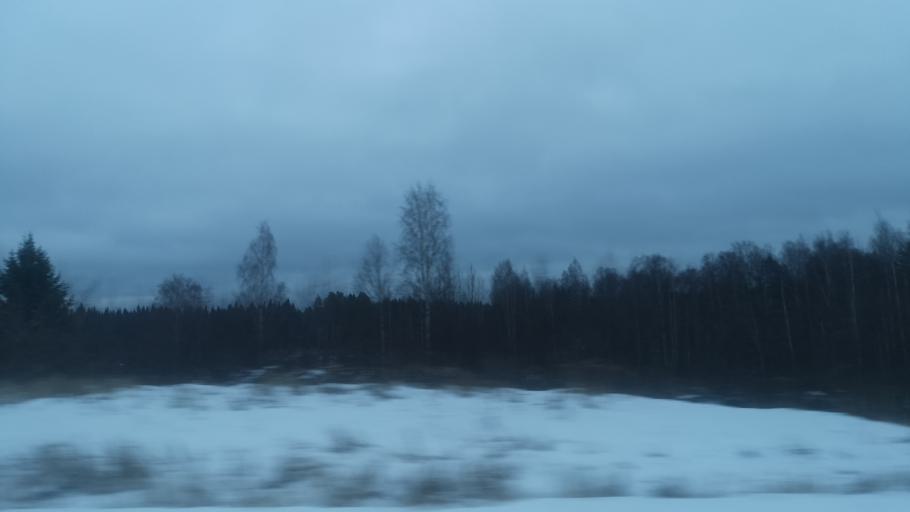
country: FI
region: Southern Savonia
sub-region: Savonlinna
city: Enonkoski
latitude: 62.1037
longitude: 28.6445
